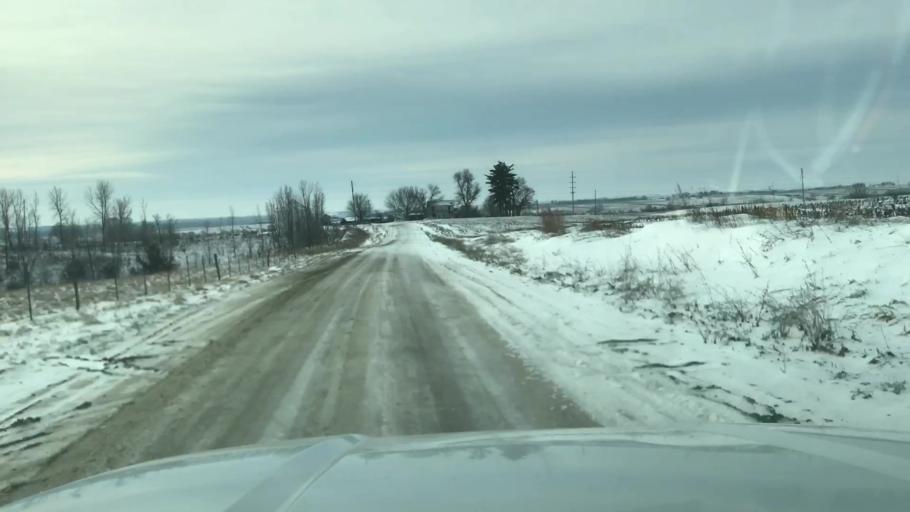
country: US
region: Missouri
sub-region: Holt County
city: Mound City
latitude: 40.1327
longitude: -95.0696
